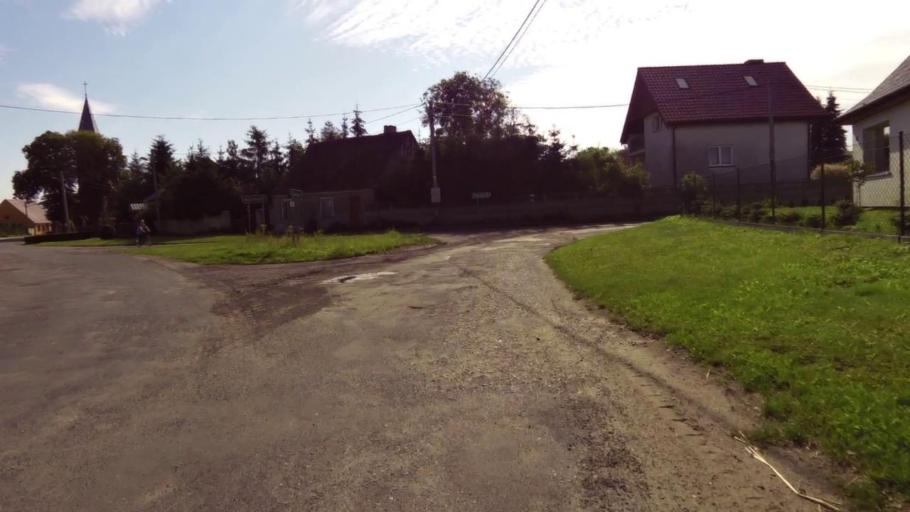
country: PL
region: West Pomeranian Voivodeship
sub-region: Powiat stargardzki
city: Marianowo
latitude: 53.3646
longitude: 15.2301
